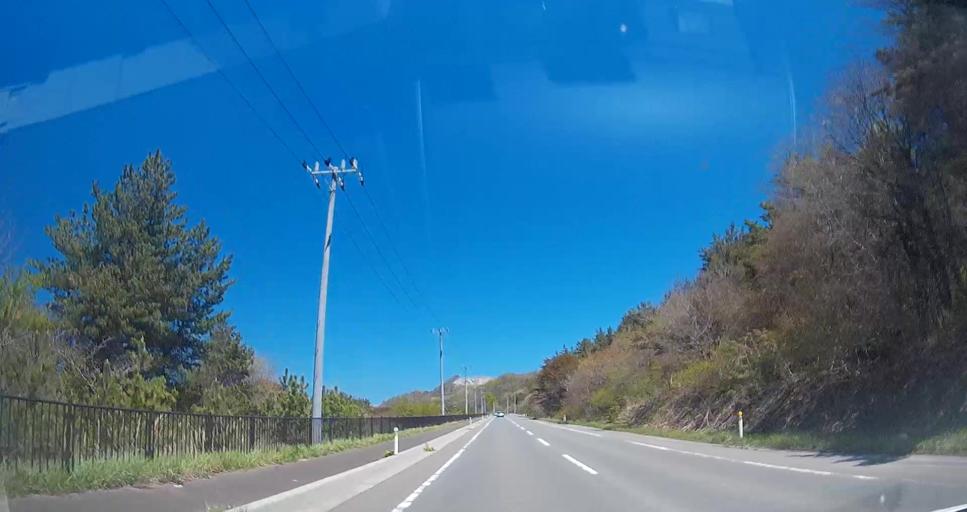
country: JP
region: Aomori
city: Mutsu
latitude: 41.3927
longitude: 141.4180
